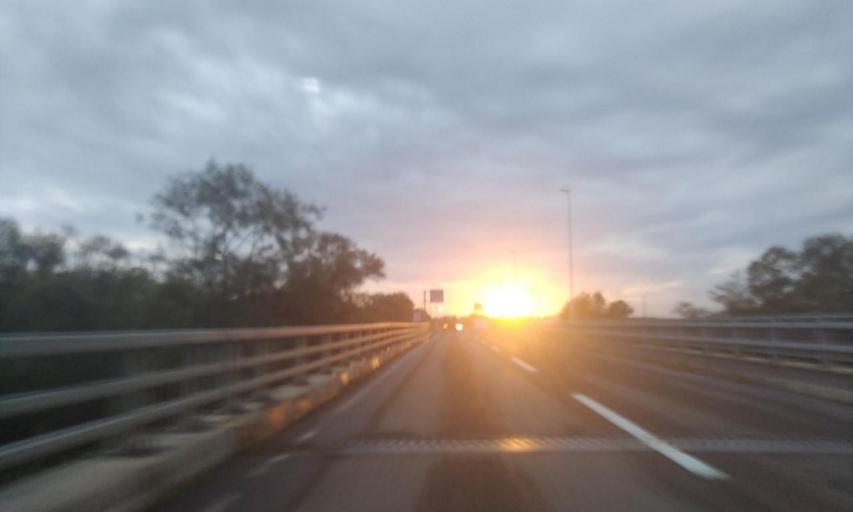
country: JP
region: Hokkaido
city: Abashiri
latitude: 43.8998
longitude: 144.6414
